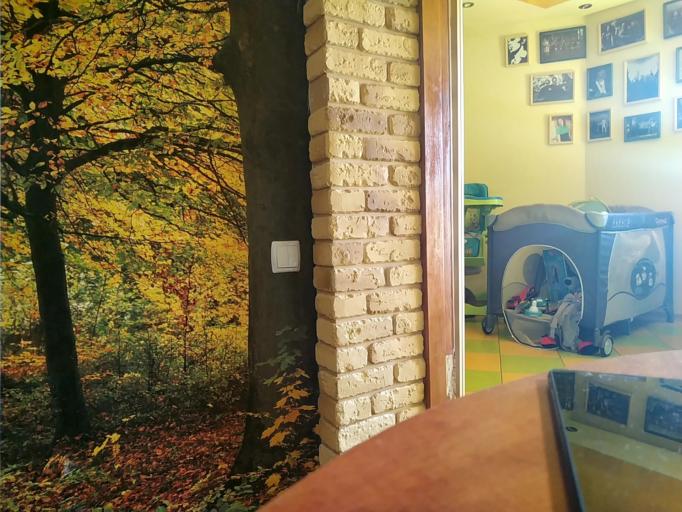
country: RU
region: Tverskaya
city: Vydropuzhsk
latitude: 57.4135
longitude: 34.7807
